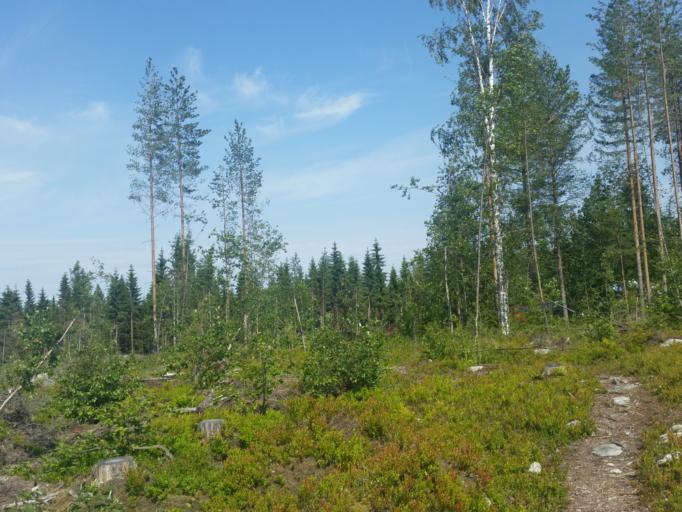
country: FI
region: Northern Savo
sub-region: Ylae-Savo
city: Keitele
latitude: 63.1040
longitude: 26.5346
